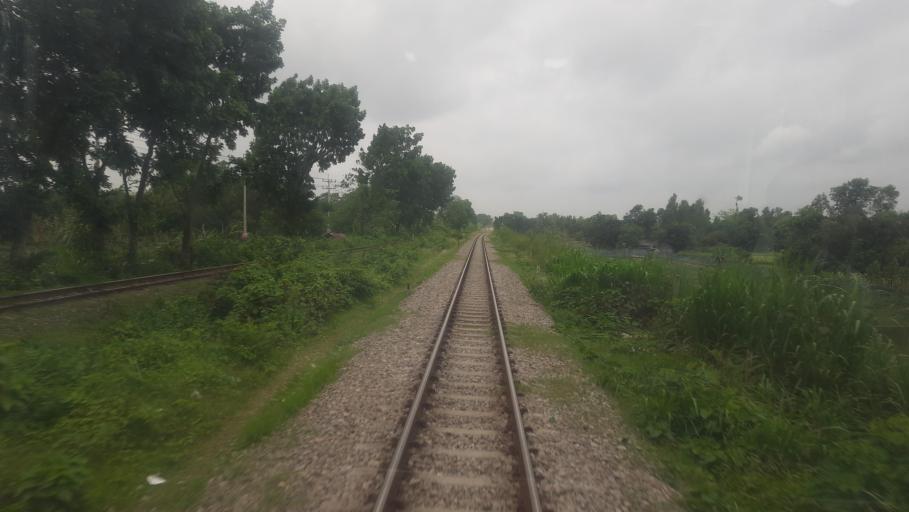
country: BD
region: Dhaka
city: Narsingdi
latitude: 23.9321
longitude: 90.7500
